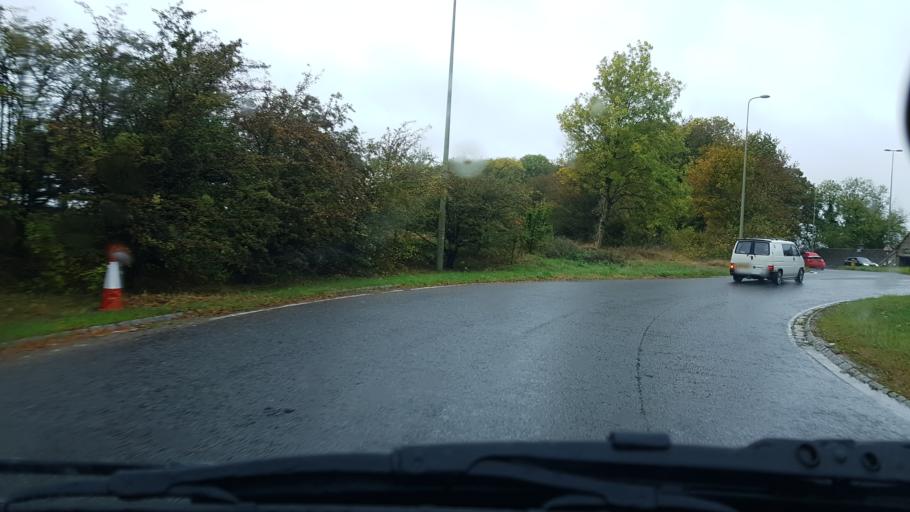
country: GB
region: England
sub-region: Oxfordshire
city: Carterton
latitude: 51.7888
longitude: -1.5828
